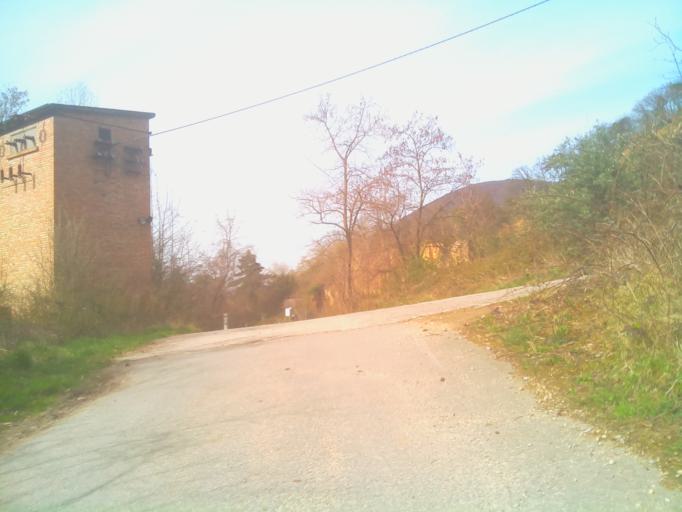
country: DE
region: Baden-Wuerttemberg
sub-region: Karlsruhe Region
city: Dossenheim
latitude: 49.4469
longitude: 8.6822
